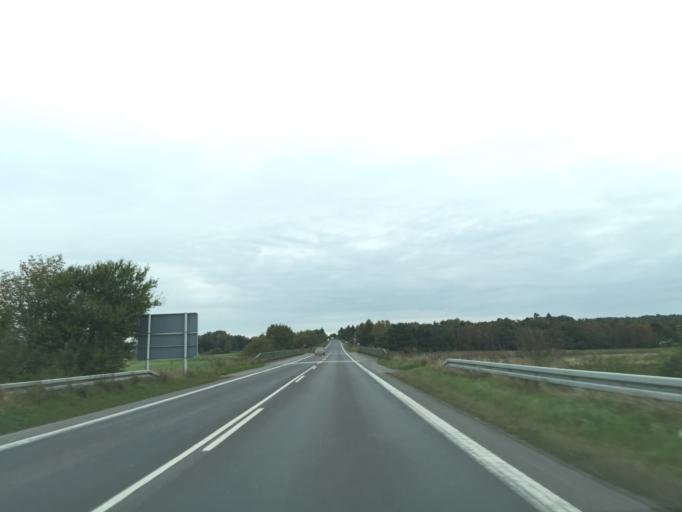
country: DK
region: Central Jutland
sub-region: Viborg Kommune
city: Bjerringbro
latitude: 56.3727
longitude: 9.6773
